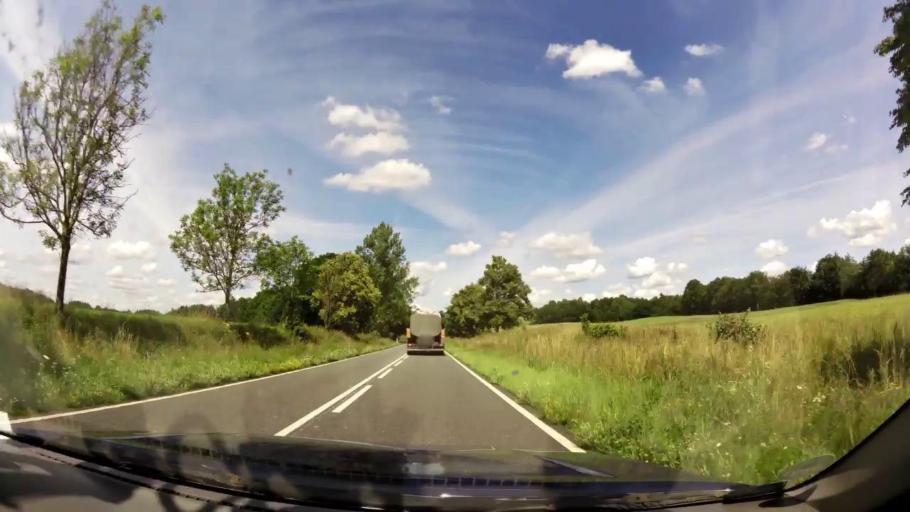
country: PL
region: West Pomeranian Voivodeship
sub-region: Powiat lobeski
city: Wegorzyno
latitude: 53.5051
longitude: 15.5756
